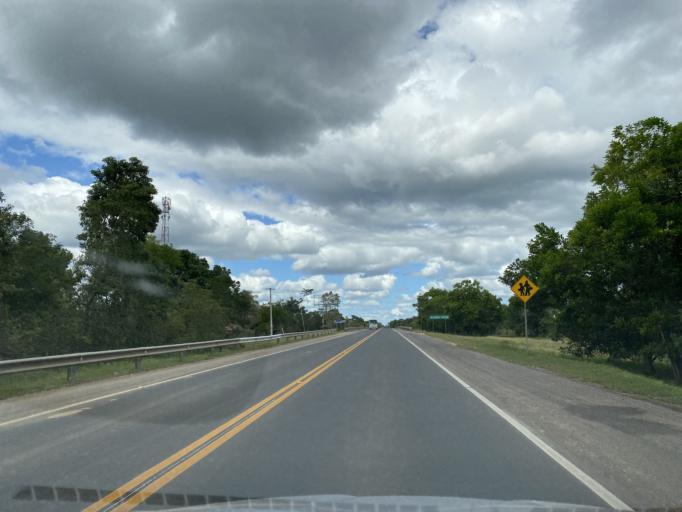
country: DO
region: Santo Domingo
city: Guerra
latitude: 18.6181
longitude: -69.7655
